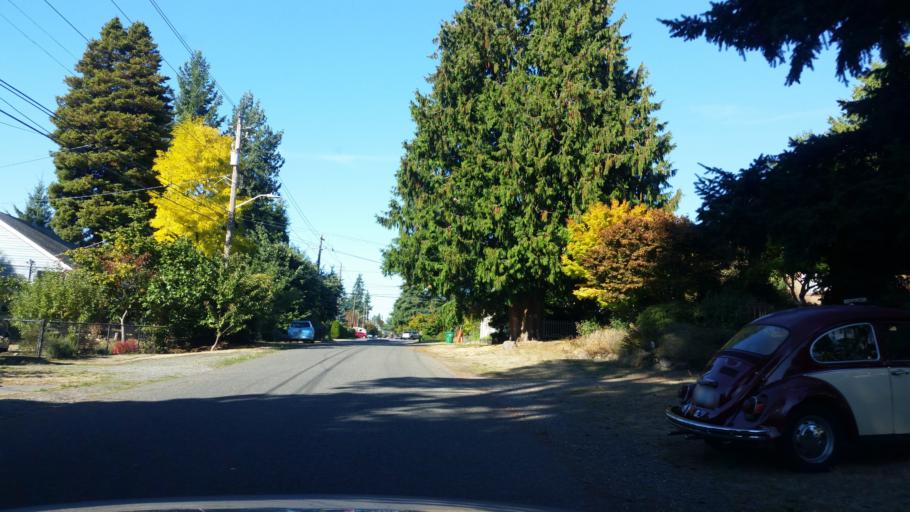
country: US
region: Washington
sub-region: King County
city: Shoreline
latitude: 47.7115
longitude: -122.3582
